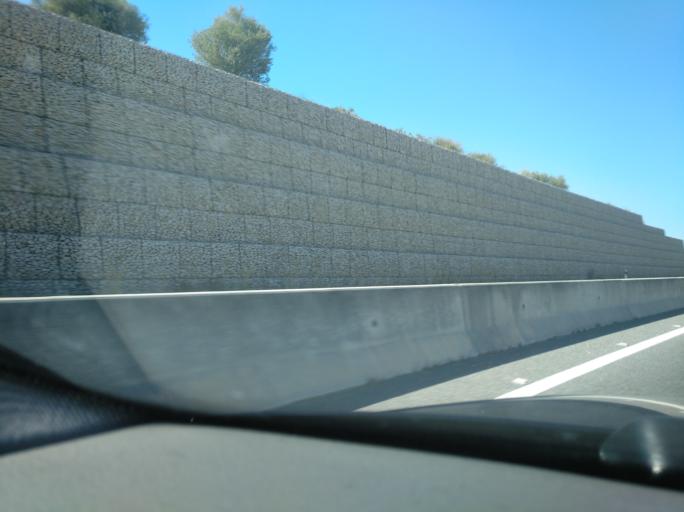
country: PT
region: Faro
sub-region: Olhao
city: Laranjeiro
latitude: 37.0681
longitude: -7.8109
